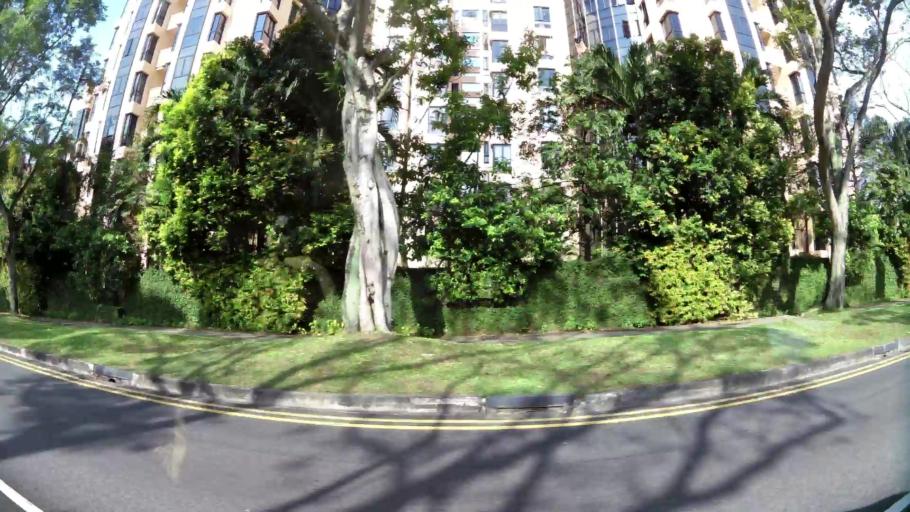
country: SG
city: Singapore
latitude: 1.3496
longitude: 103.8474
